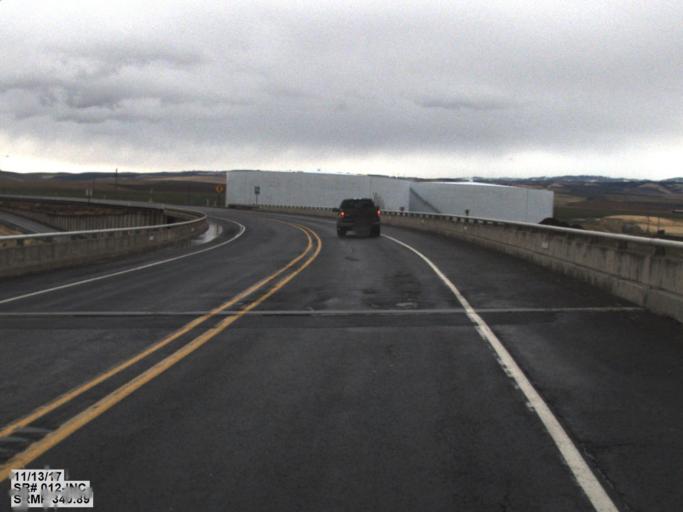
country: US
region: Washington
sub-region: Walla Walla County
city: Walla Walla East
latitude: 46.0879
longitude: -118.2610
